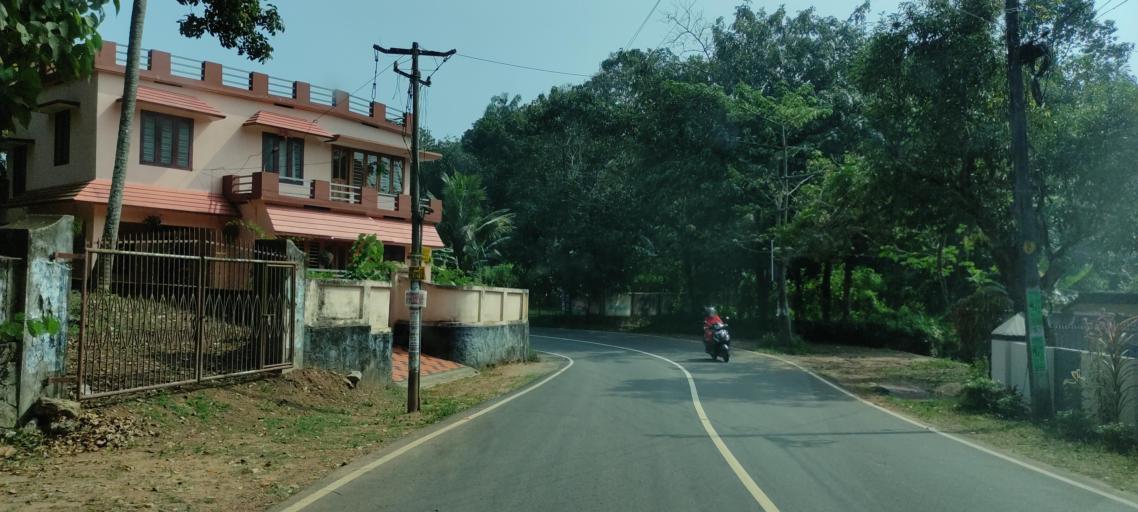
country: IN
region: Kerala
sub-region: Pattanamtitta
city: Adur
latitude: 9.2404
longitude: 76.6831
